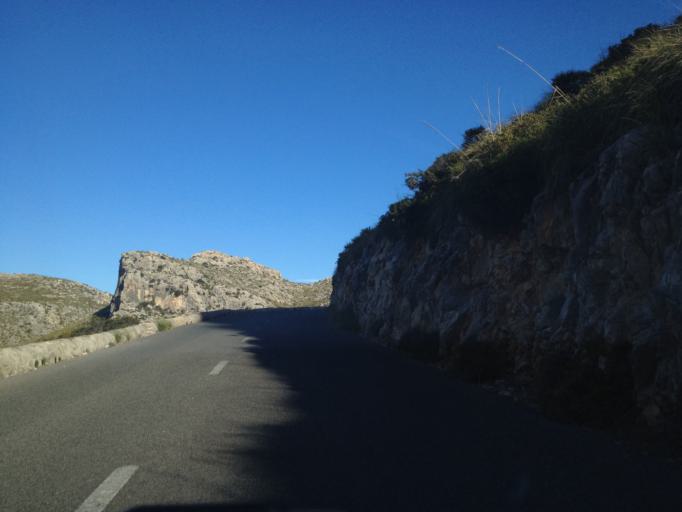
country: ES
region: Balearic Islands
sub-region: Illes Balears
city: Alcudia
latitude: 39.9204
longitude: 3.1070
